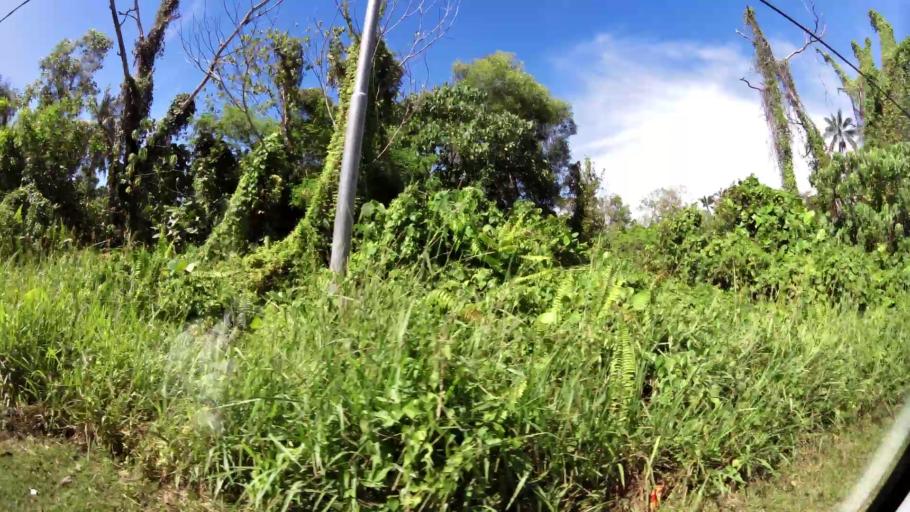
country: BN
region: Brunei and Muara
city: Bandar Seri Begawan
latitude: 5.0031
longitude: 115.0619
